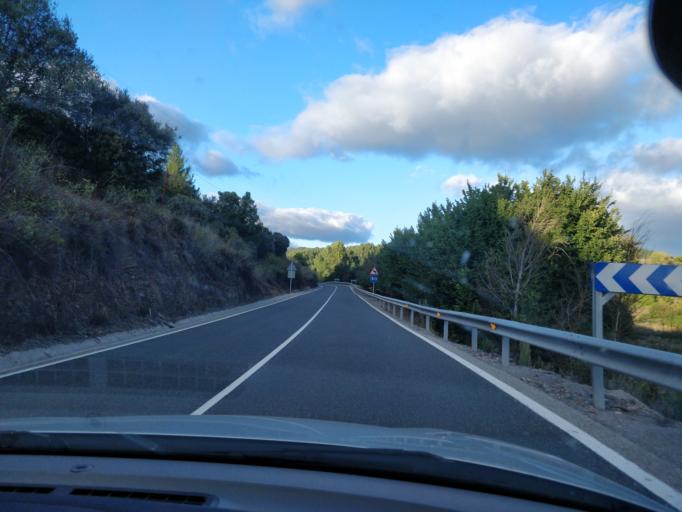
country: ES
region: Castille and Leon
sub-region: Provincia de Leon
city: Borrenes
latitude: 42.4909
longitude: -6.7427
